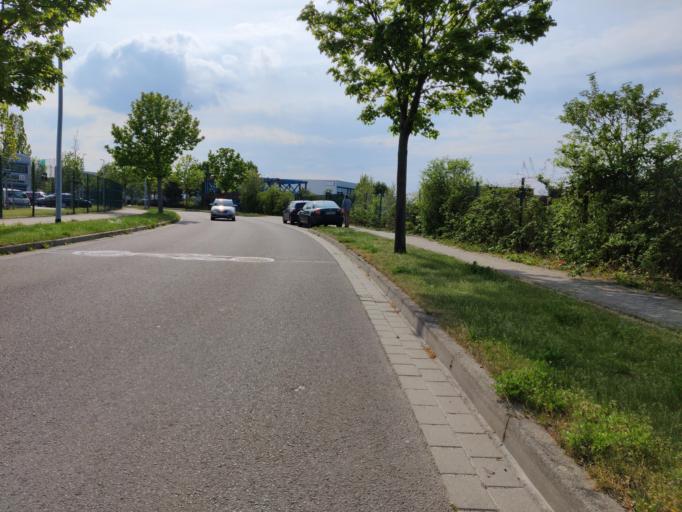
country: DE
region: Saxony
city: Zwenkau
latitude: 51.2114
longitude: 12.3360
